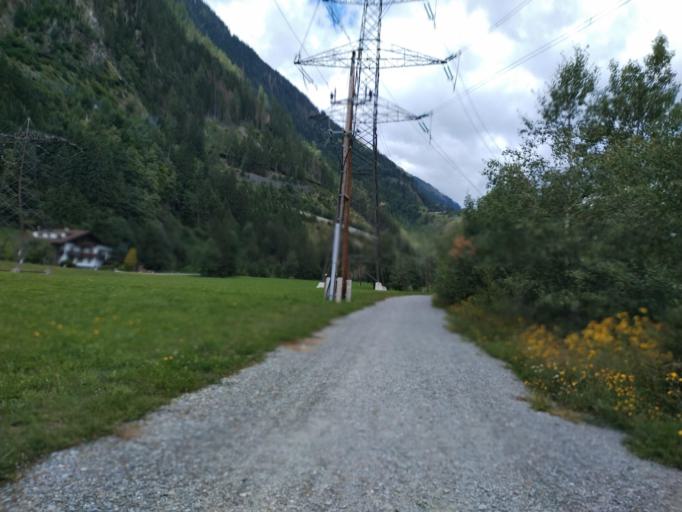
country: AT
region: Tyrol
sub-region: Politischer Bezirk Lienz
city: Hopfgarten in Defereggen
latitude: 46.9295
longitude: 12.5784
